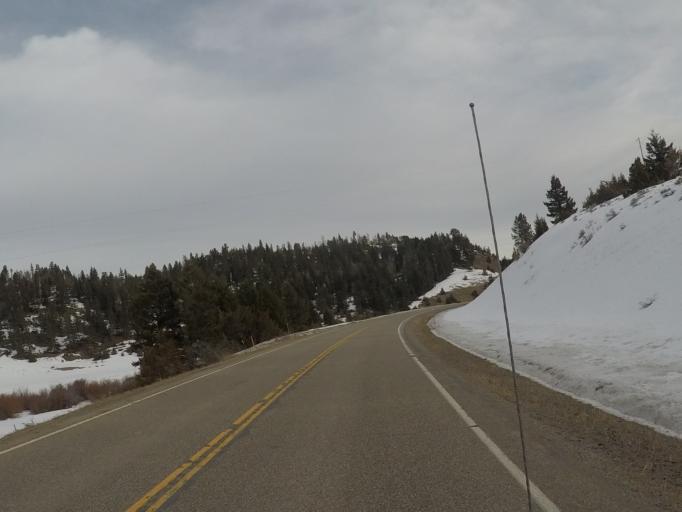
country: US
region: Montana
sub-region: Meagher County
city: White Sulphur Springs
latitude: 46.6766
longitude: -110.8780
